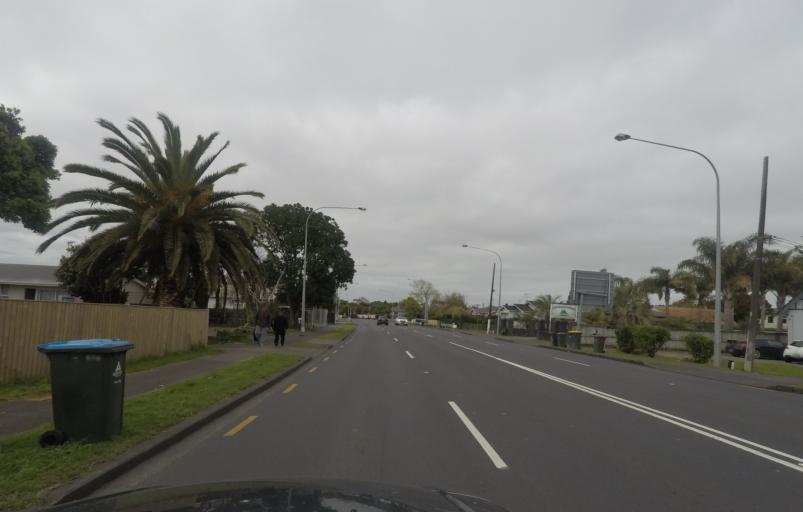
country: NZ
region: Auckland
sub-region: Auckland
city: Wiri
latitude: -36.9514
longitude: 174.8453
